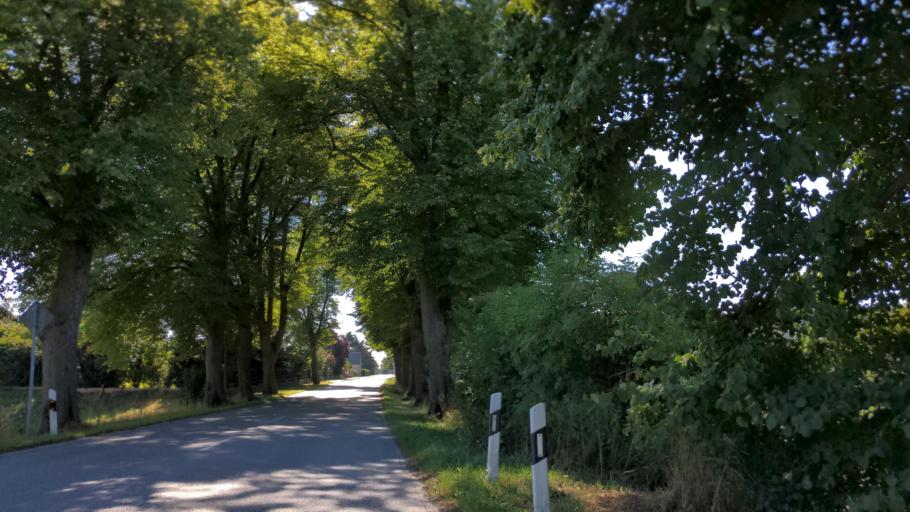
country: DE
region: Mecklenburg-Vorpommern
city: Selmsdorf
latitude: 53.8543
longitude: 10.9210
